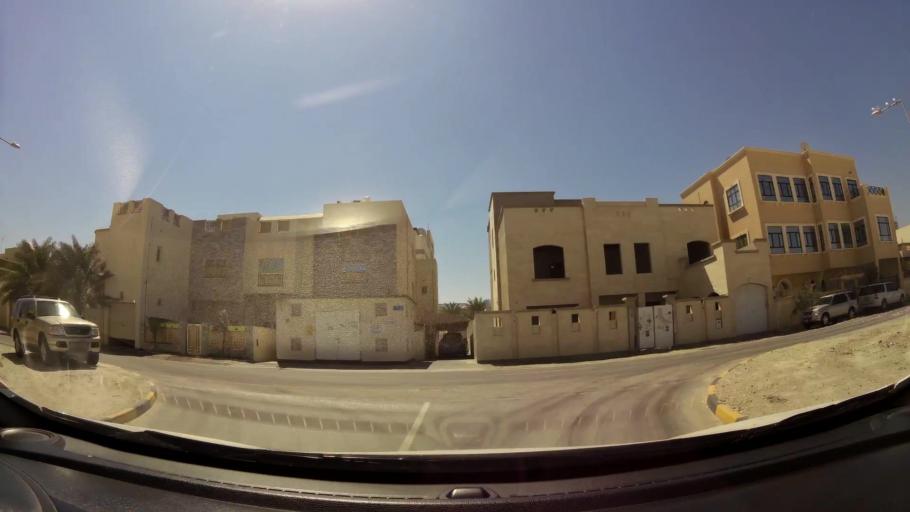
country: BH
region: Muharraq
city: Al Muharraq
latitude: 26.2787
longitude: 50.6018
